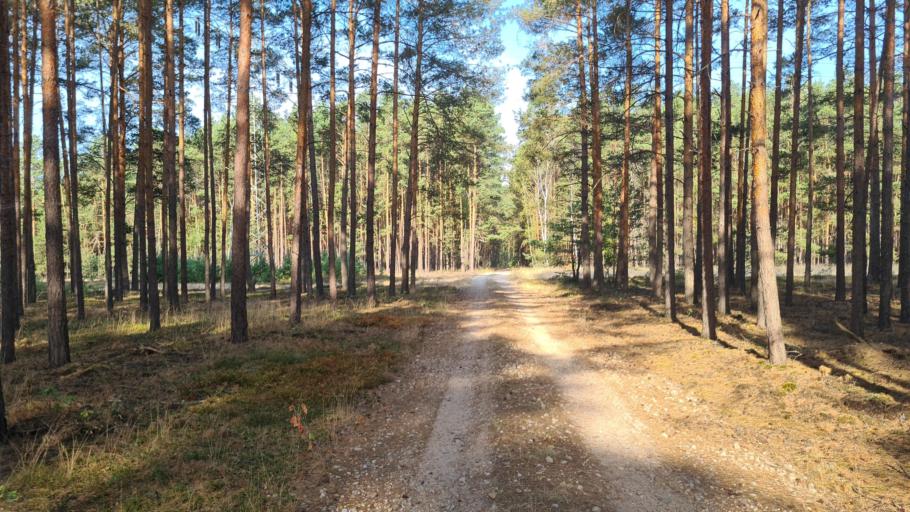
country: DE
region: Brandenburg
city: Crinitz
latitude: 51.6742
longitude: 13.7597
